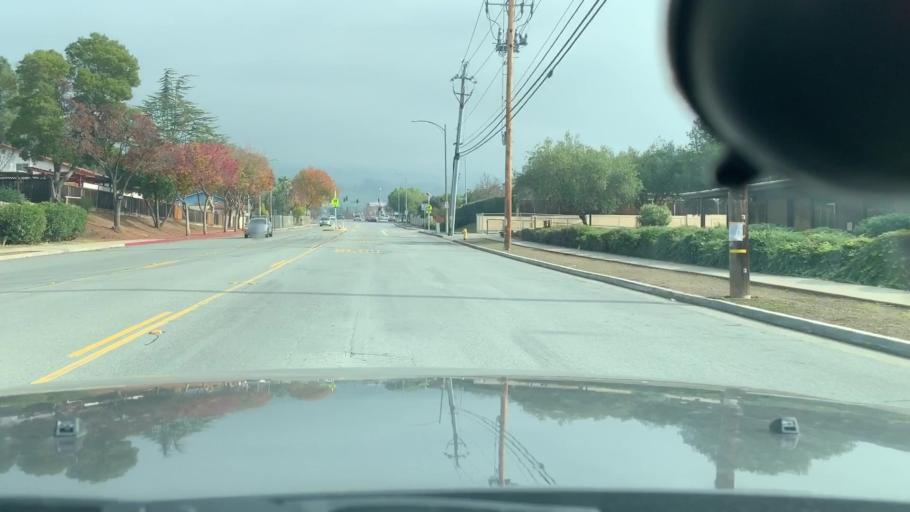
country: US
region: California
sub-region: Santa Clara County
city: Alum Rock
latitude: 37.3248
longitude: -121.7850
